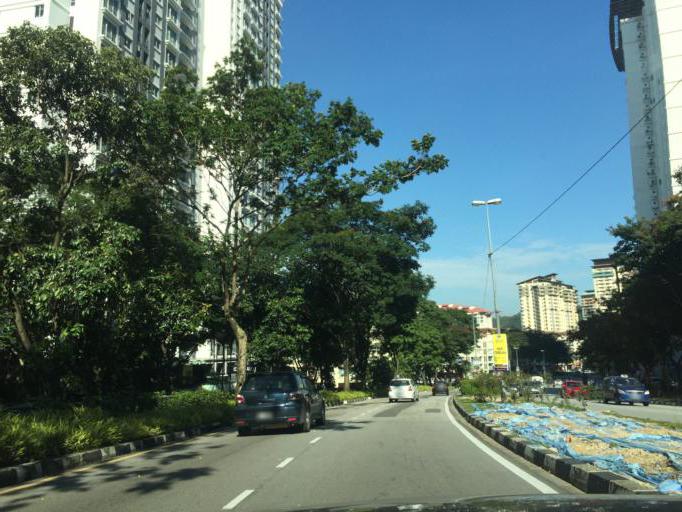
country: MY
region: Selangor
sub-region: Petaling
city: Petaling Jaya
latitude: 3.1647
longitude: 101.6098
